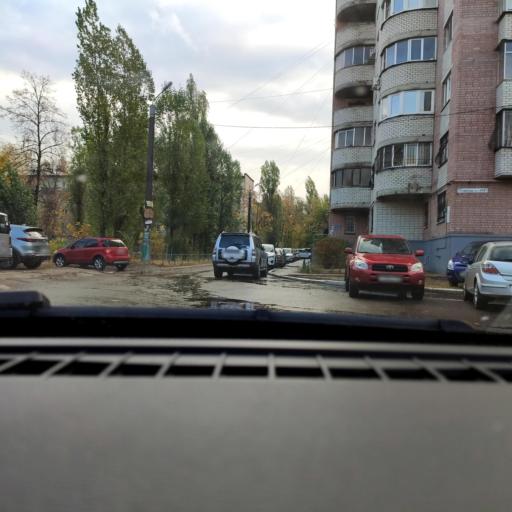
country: RU
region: Voronezj
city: Voronezh
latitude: 51.6828
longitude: 39.2655
